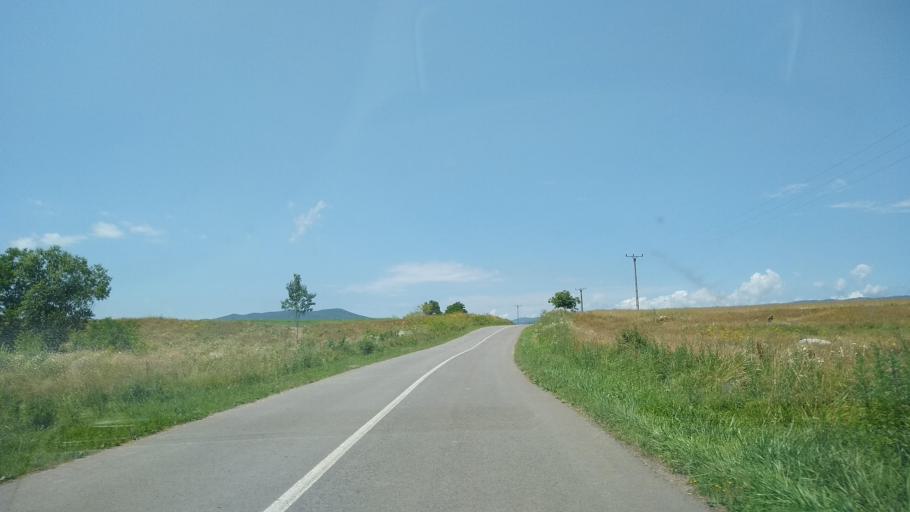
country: RO
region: Hunedoara
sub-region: Comuna Totesti
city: Totesti
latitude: 45.5775
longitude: 22.8539
